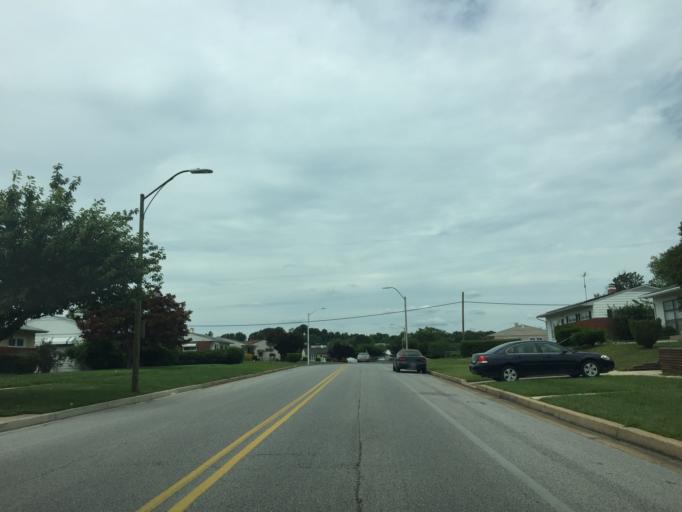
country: US
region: Maryland
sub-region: Baltimore County
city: Parkville
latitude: 39.3623
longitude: -76.5687
